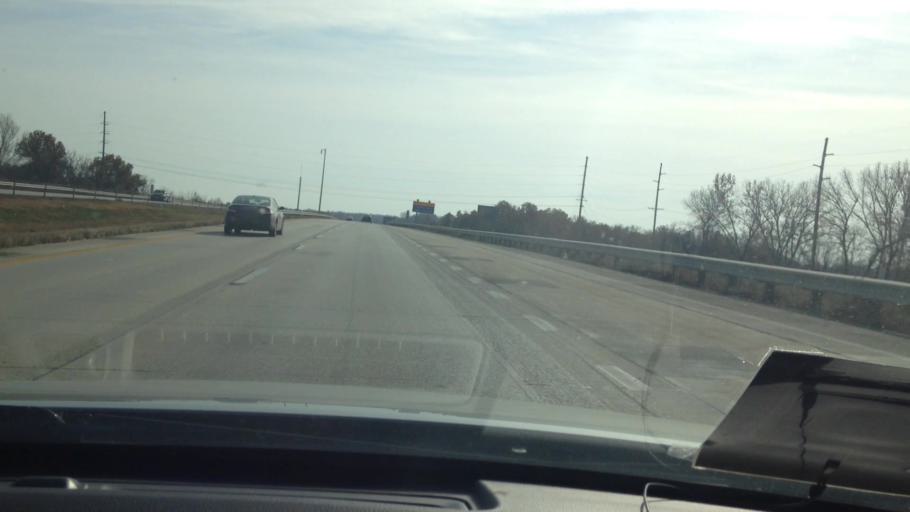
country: US
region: Missouri
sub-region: Cass County
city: Harrisonville
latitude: 38.6470
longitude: -94.3636
